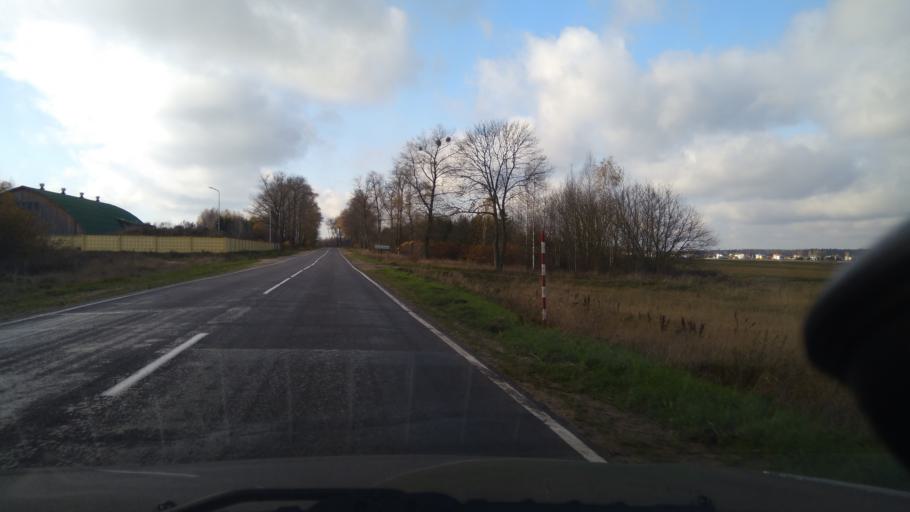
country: BY
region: Minsk
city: Slutsk
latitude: 53.2204
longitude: 27.5604
